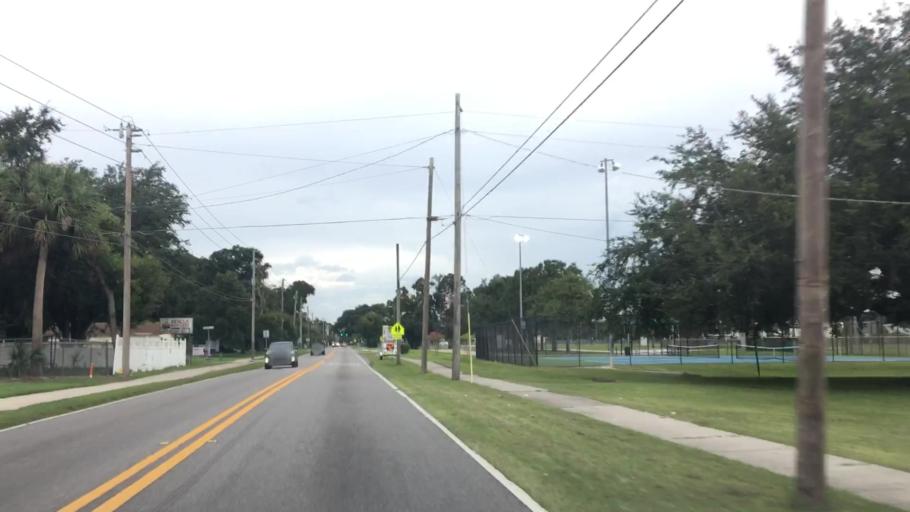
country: US
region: Florida
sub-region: Seminole County
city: Sanford
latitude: 28.8013
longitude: -81.2516
